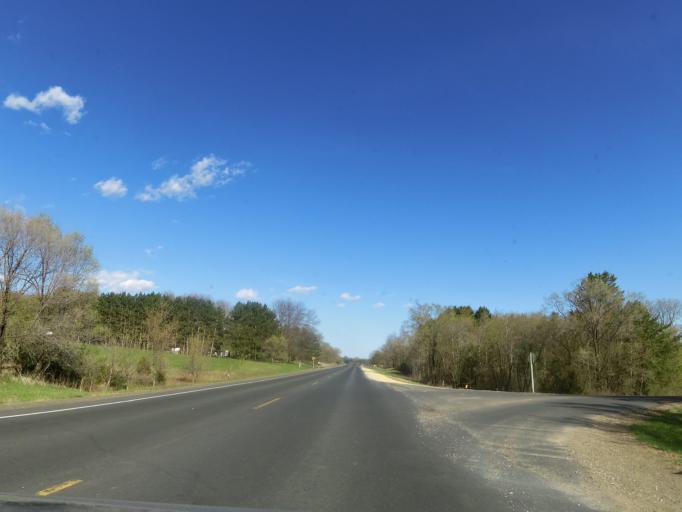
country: US
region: Wisconsin
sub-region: Saint Croix County
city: North Hudson
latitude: 45.0492
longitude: -92.7166
